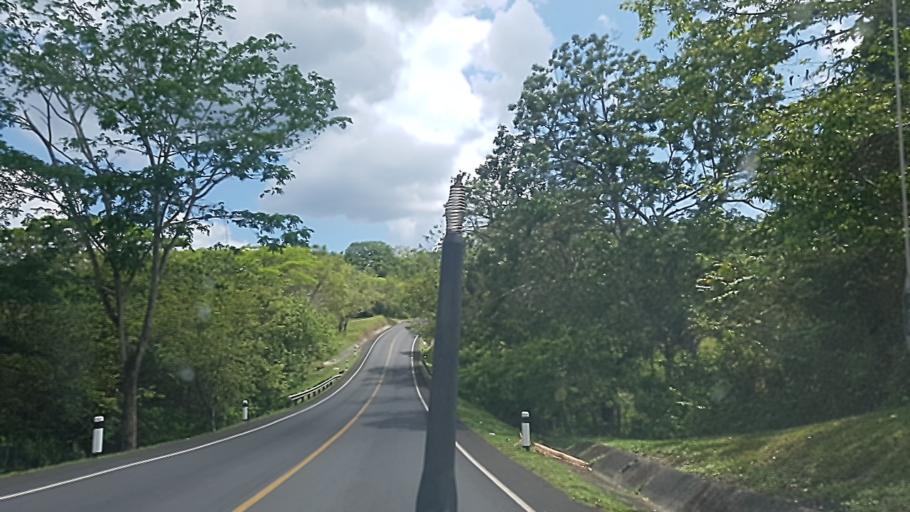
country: NI
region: Atlantico Sur
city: Muelle de los Bueyes
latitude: 11.9850
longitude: -84.7569
